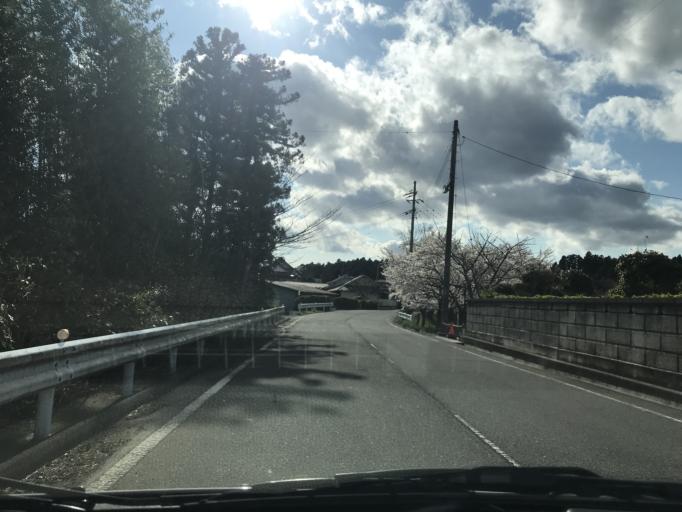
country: JP
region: Miyagi
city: Wakuya
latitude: 38.6095
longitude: 141.2387
